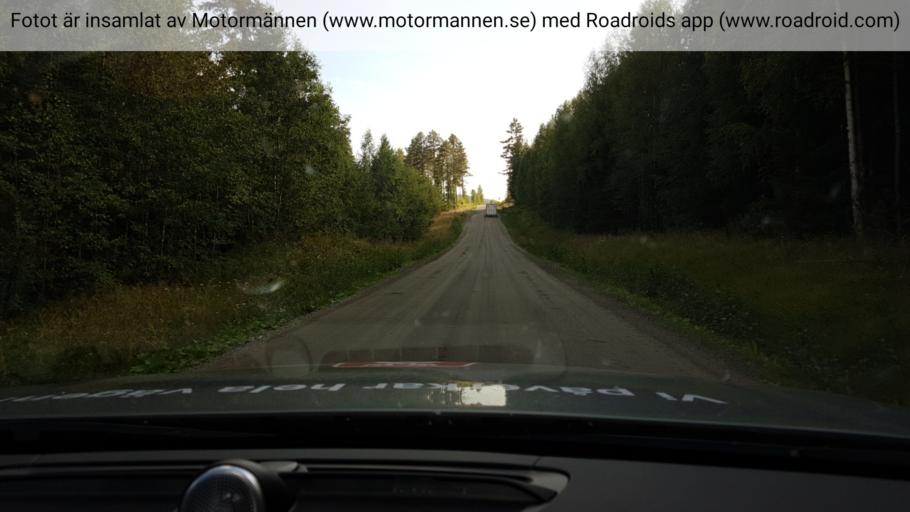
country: SE
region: Vaesternorrland
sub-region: Solleftea Kommun
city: As
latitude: 63.7890
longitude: 16.3916
